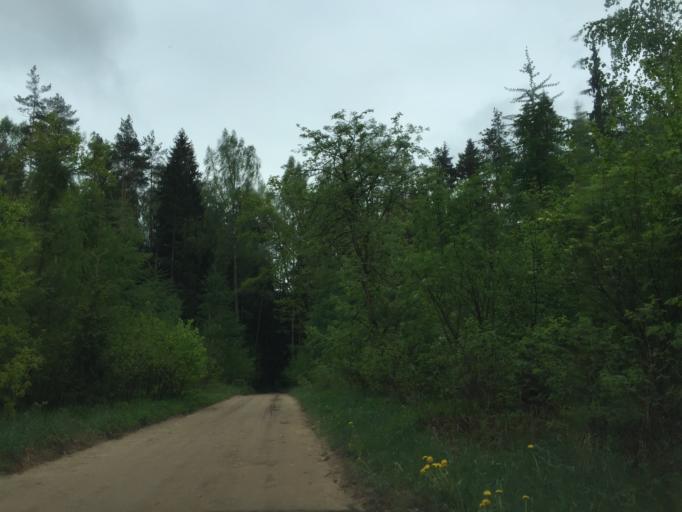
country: LV
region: Kegums
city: Kegums
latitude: 56.7375
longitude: 24.7411
